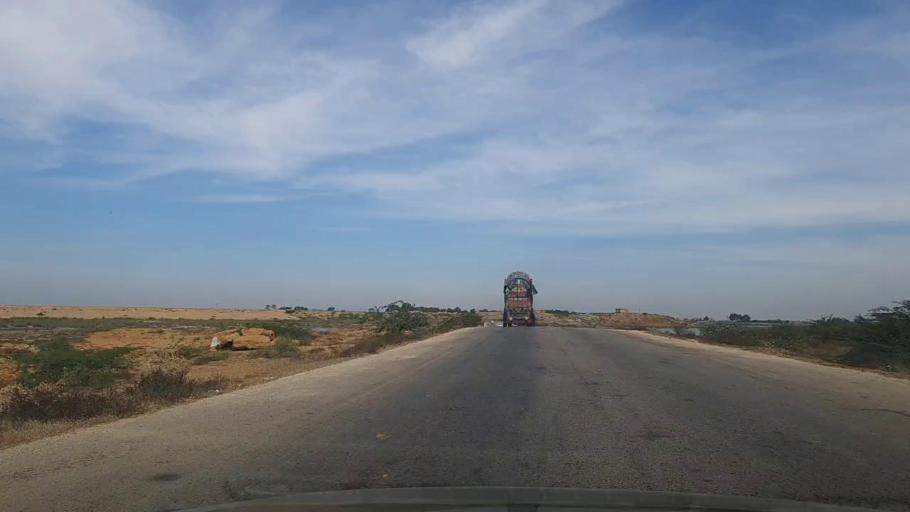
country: PK
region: Sindh
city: Daro Mehar
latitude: 24.9063
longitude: 68.0698
